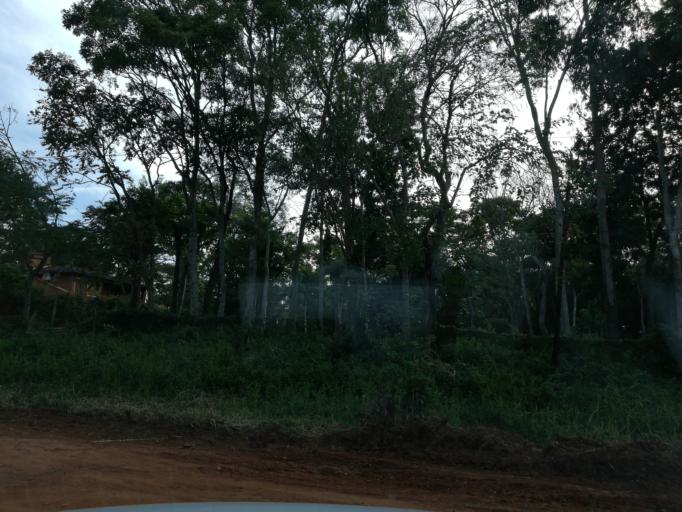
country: AR
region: Misiones
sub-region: Departamento de Capital
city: Posadas
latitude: -27.3557
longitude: -55.9300
